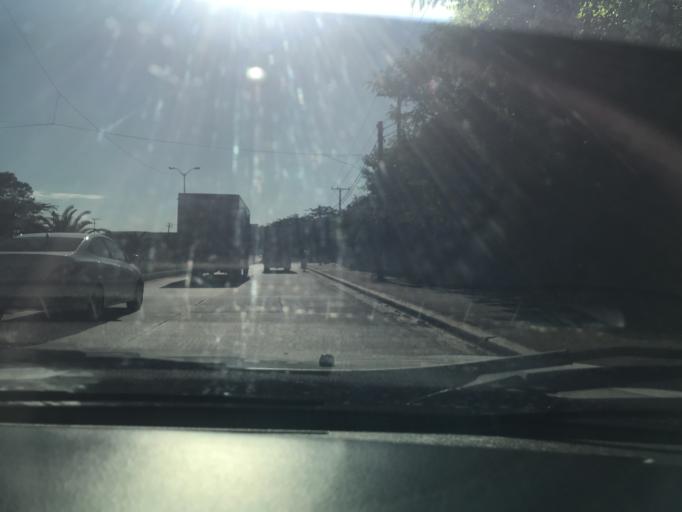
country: DO
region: Santiago
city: Santiago de los Caballeros
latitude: 19.4248
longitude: -70.6672
